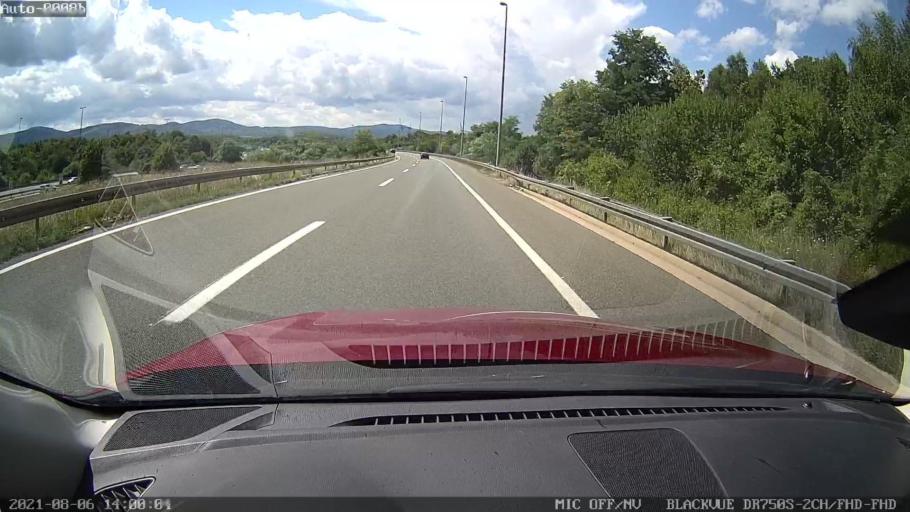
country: HR
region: Karlovacka
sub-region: Grad Ogulin
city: Ogulin
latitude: 45.4087
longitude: 15.2620
